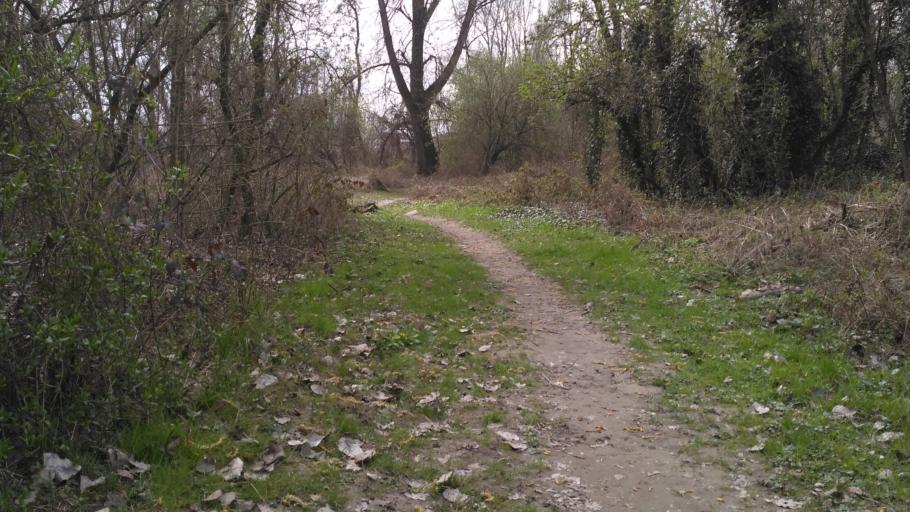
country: IT
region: Piedmont
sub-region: Provincia di Cuneo
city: Savigliano
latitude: 44.6617
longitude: 7.6556
